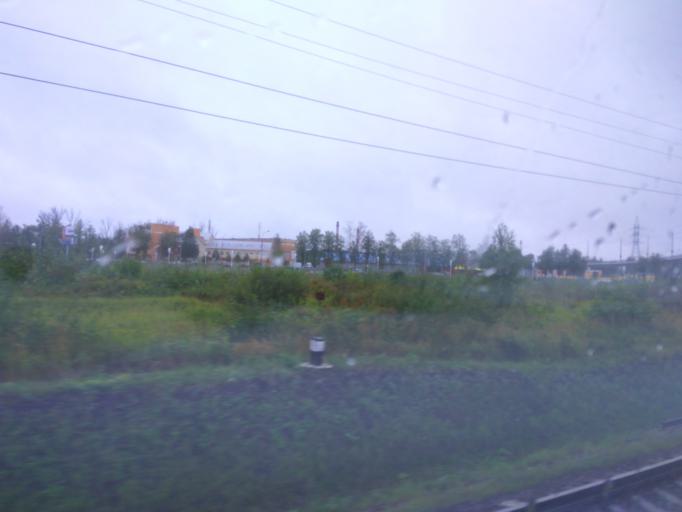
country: RU
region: Moskovskaya
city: Stupino
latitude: 54.9031
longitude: 38.0844
